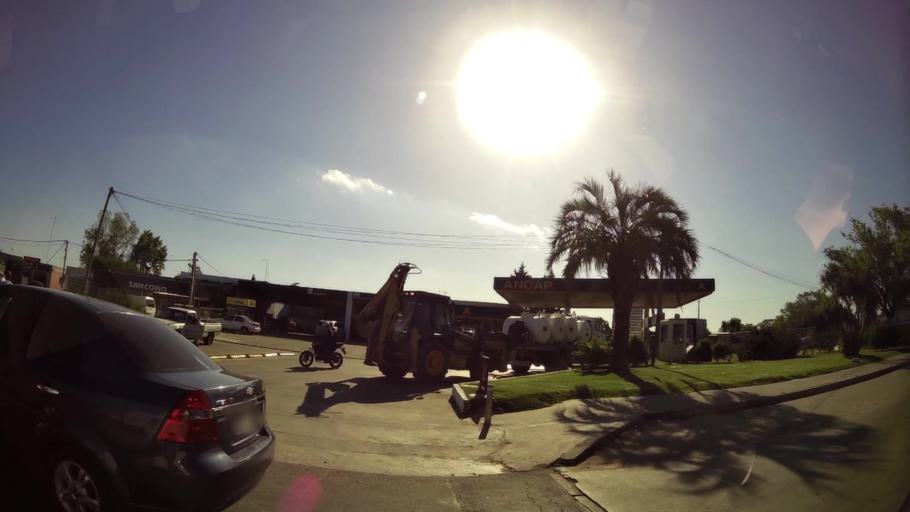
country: UY
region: Canelones
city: La Paz
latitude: -34.8066
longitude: -56.1612
